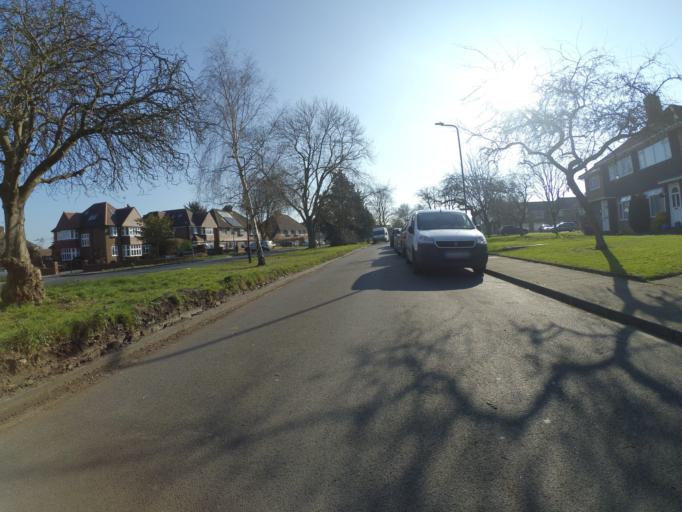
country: GB
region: England
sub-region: Greater London
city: Wembley
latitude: 51.5745
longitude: -0.2680
